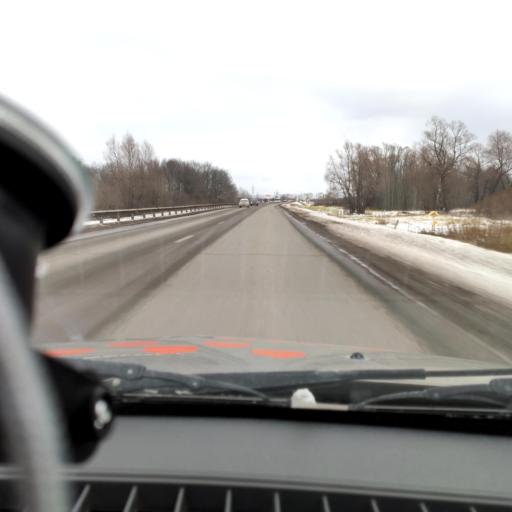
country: RU
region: Bashkortostan
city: Mikhaylovka
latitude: 54.8235
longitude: 55.8338
